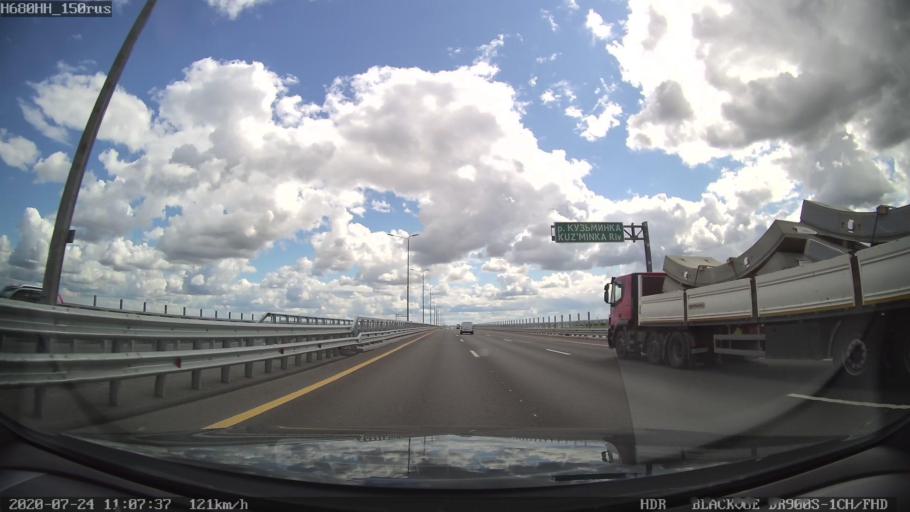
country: RU
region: St.-Petersburg
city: Pushkin
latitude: 59.7555
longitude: 30.4127
